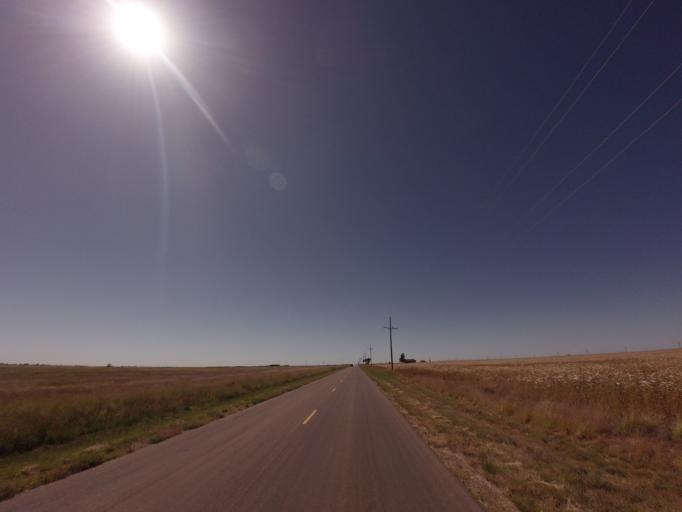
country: US
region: New Mexico
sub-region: Curry County
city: Clovis
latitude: 34.4484
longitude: -103.2184
